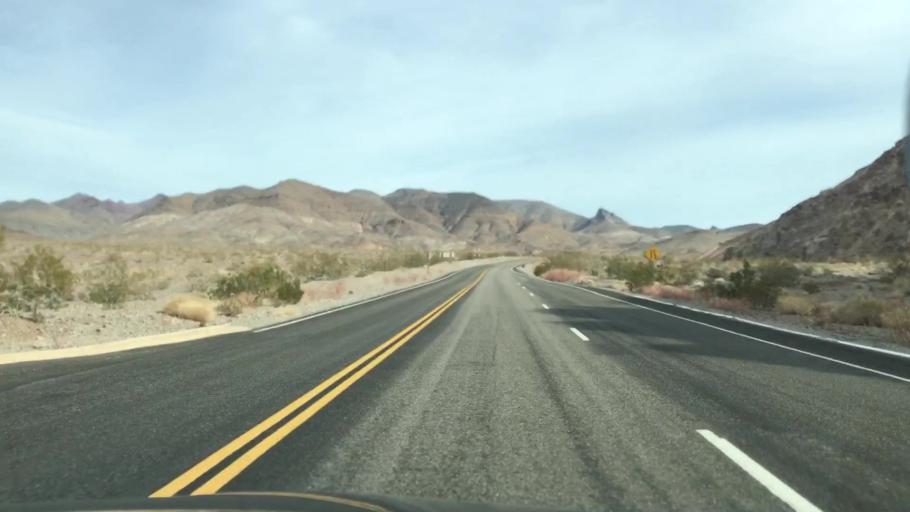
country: US
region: Nevada
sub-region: Nye County
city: Beatty
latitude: 36.7245
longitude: -116.9775
